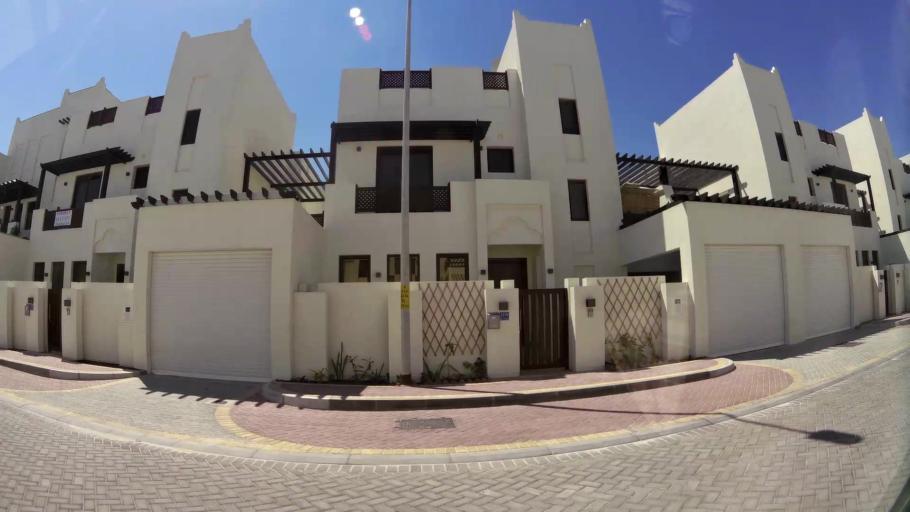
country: BH
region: Muharraq
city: Al Muharraq
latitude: 26.3012
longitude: 50.6388
